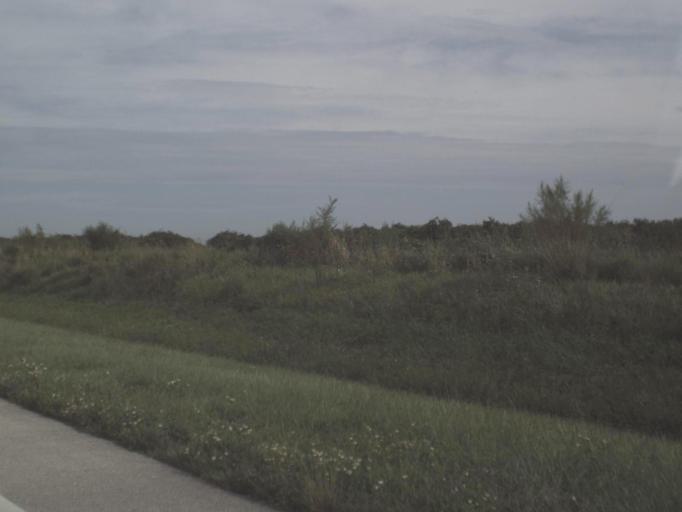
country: US
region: Florida
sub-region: DeSoto County
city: Nocatee
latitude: 27.0641
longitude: -81.7916
